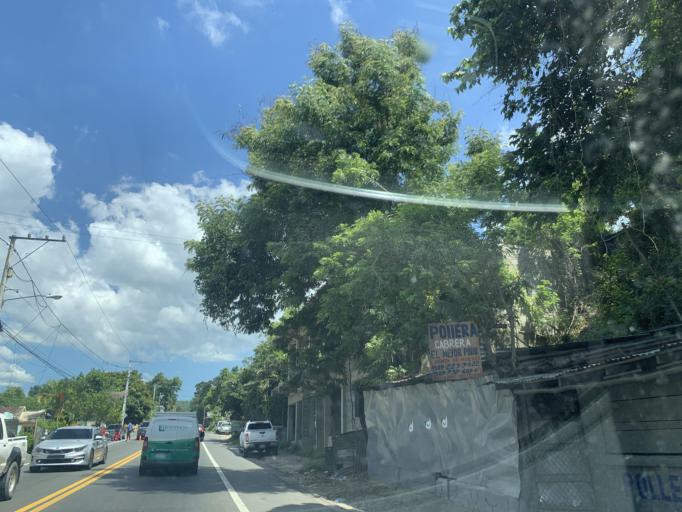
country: DO
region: Puerto Plata
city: Altamira
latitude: 19.6727
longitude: -70.8348
